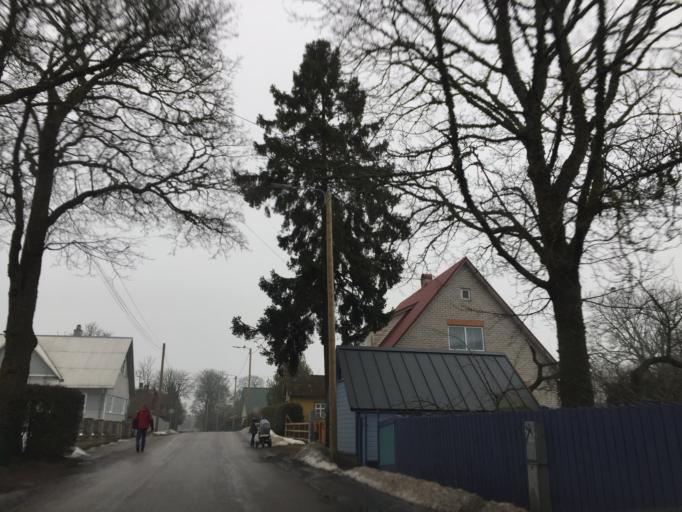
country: EE
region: Saare
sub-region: Kuressaare linn
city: Kuressaare
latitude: 58.2491
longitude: 22.4860
